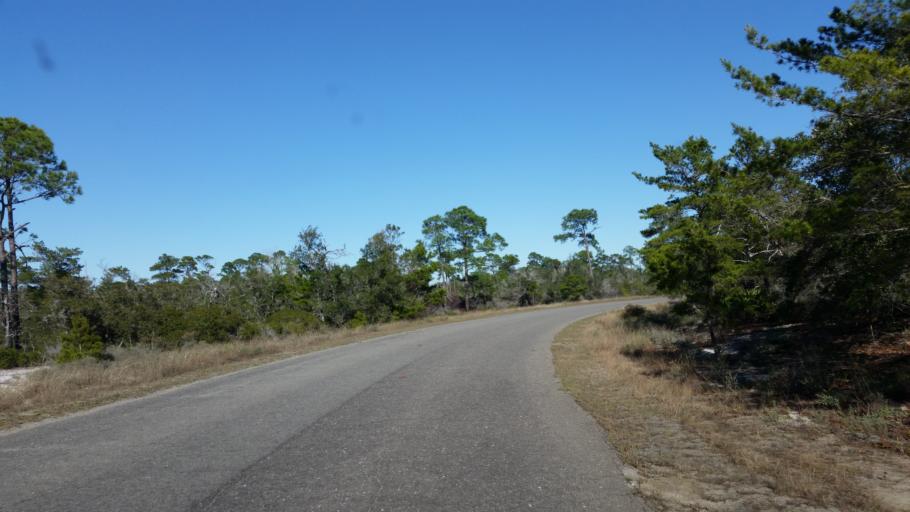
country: US
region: Alabama
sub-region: Baldwin County
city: Orange Beach
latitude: 30.3145
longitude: -87.4209
